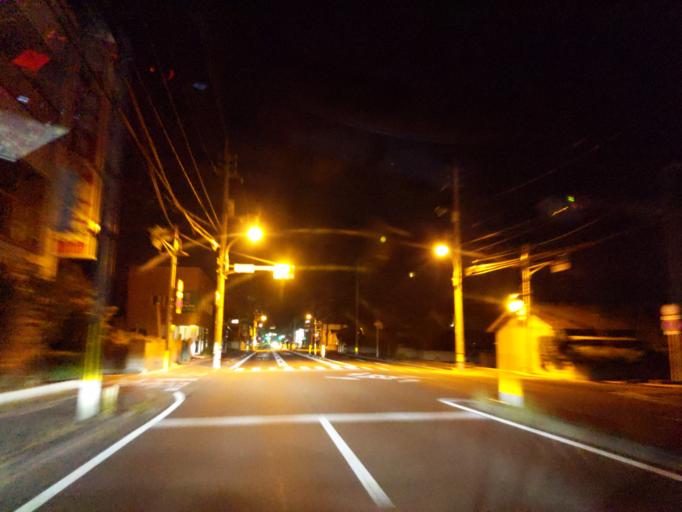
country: JP
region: Okayama
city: Okayama-shi
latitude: 34.6767
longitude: 133.9586
